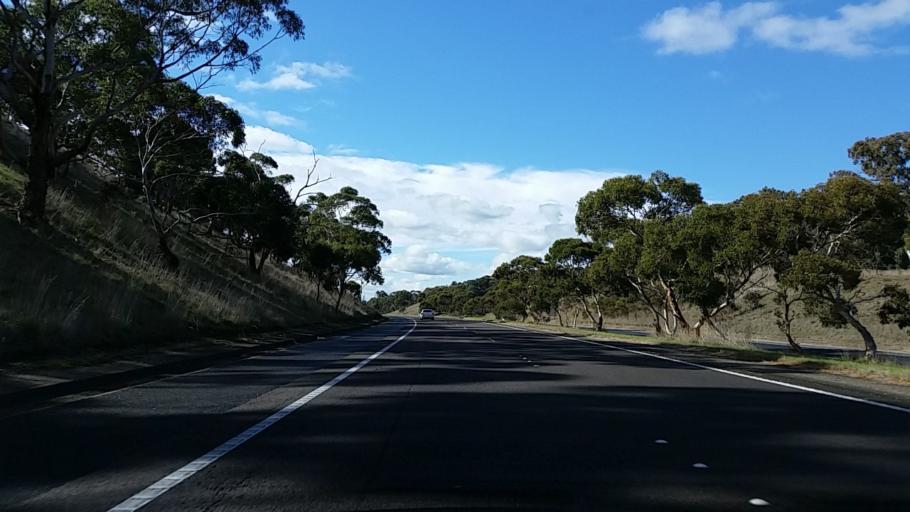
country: AU
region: South Australia
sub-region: Mount Barker
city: Nairne
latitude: -35.0577
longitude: 138.9120
